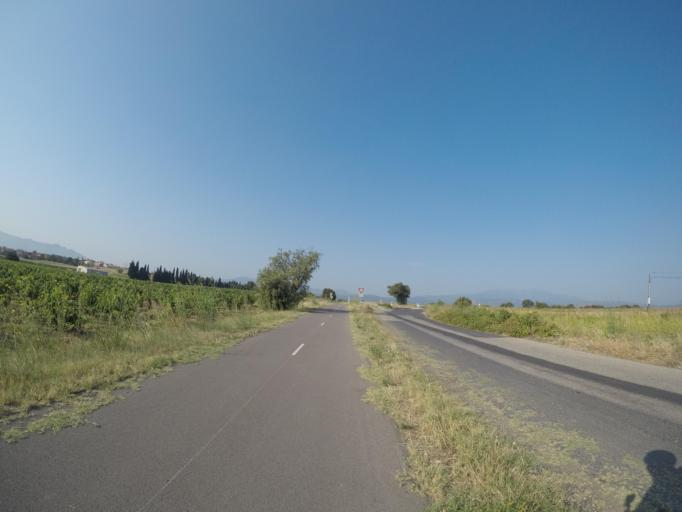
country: FR
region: Languedoc-Roussillon
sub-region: Departement des Pyrenees-Orientales
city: Ponteilla
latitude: 42.6353
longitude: 2.8088
